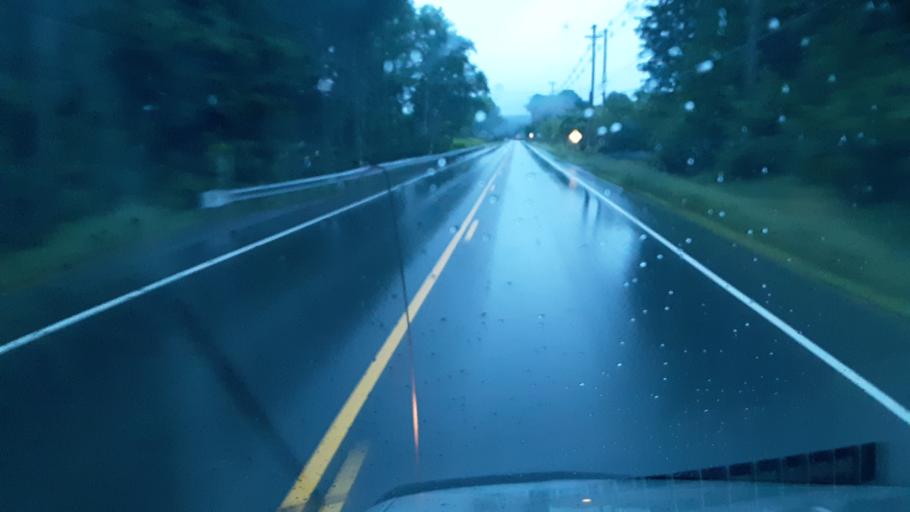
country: US
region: Maine
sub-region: Penobscot County
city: Patten
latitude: 45.8815
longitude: -68.4180
